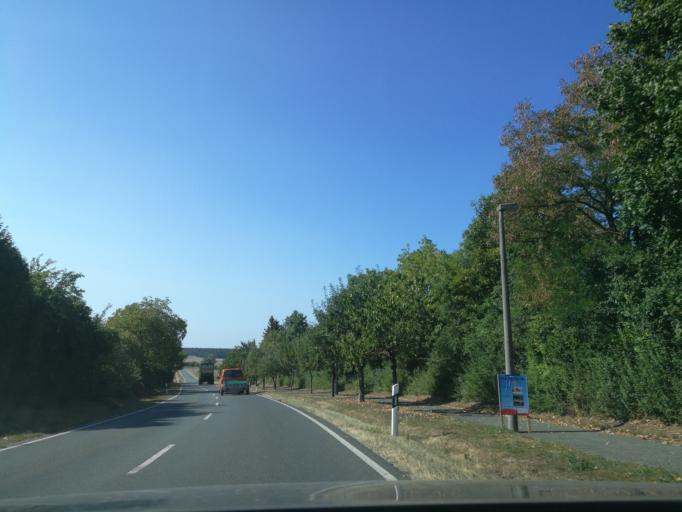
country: DE
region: Bavaria
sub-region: Regierungsbezirk Mittelfranken
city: Cadolzburg
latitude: 49.4536
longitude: 10.8498
